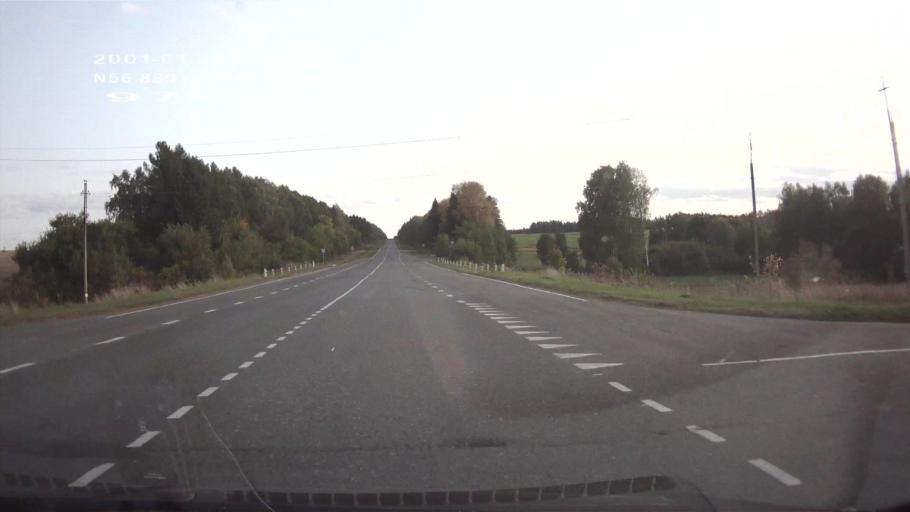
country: RU
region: Mariy-El
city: Kuzhener
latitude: 56.8879
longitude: 48.7519
